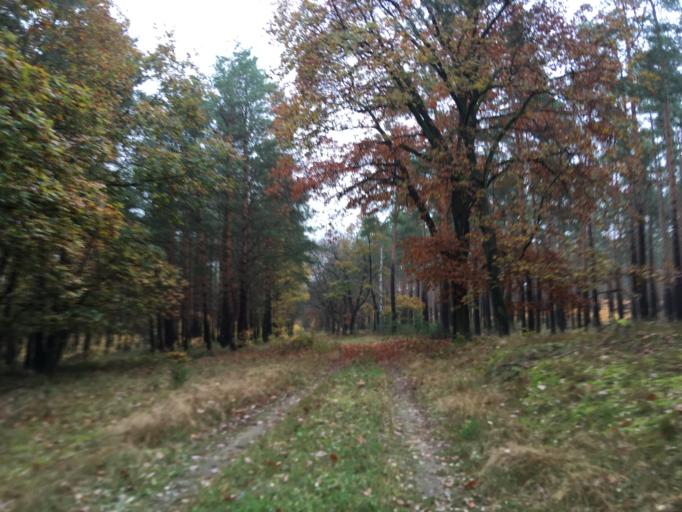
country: DE
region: Brandenburg
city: Briesen
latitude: 52.2577
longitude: 14.2942
